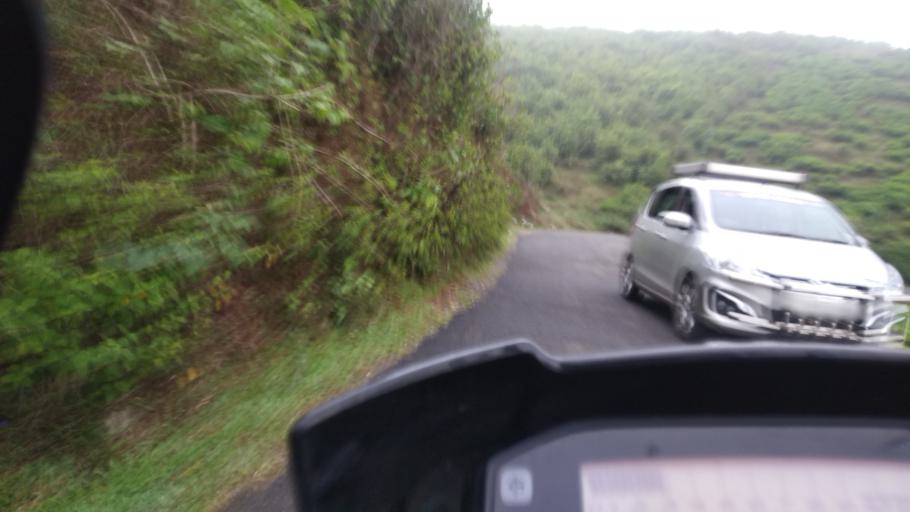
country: IN
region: Kerala
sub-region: Kottayam
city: Erattupetta
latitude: 9.6320
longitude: 76.9430
